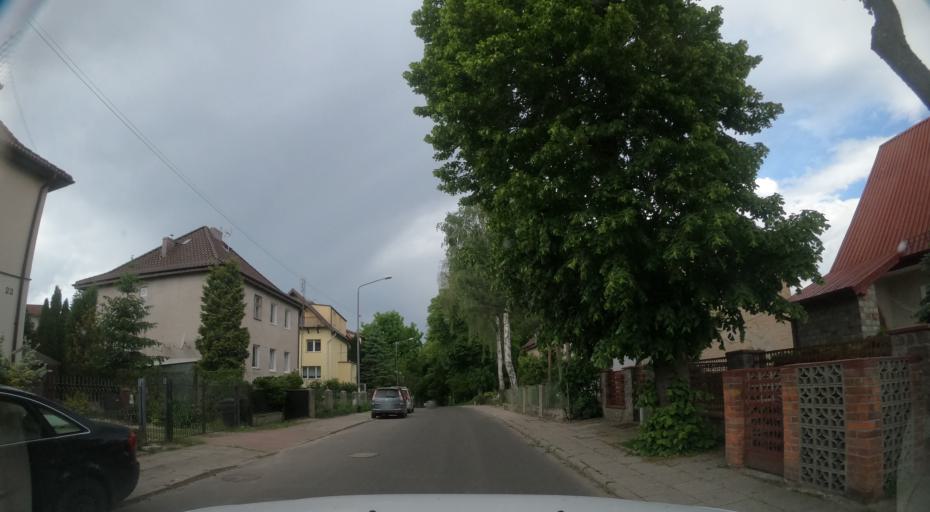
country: PL
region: West Pomeranian Voivodeship
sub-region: Szczecin
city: Szczecin
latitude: 53.3634
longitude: 14.6052
